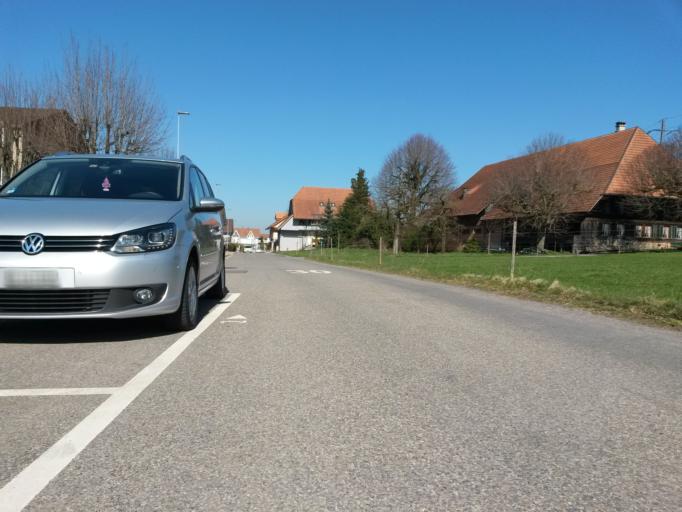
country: CH
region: Bern
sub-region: Bern-Mittelland District
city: Zollikofen
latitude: 47.0130
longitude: 7.4761
